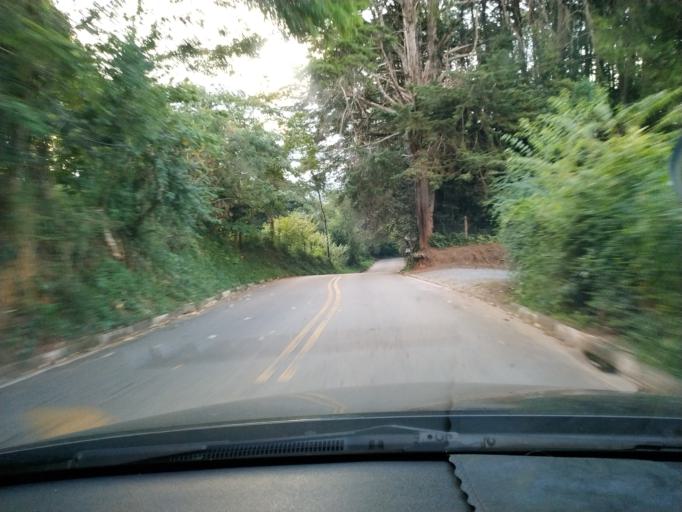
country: BR
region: Sao Paulo
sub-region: Campos Do Jordao
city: Campos do Jordao
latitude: -22.8058
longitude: -45.6344
